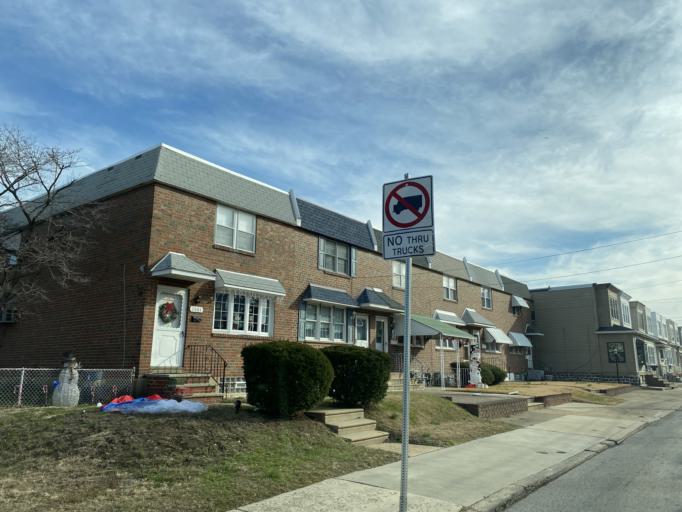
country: US
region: New Jersey
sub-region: Camden County
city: Pennsauken
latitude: 39.9984
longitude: -75.0790
